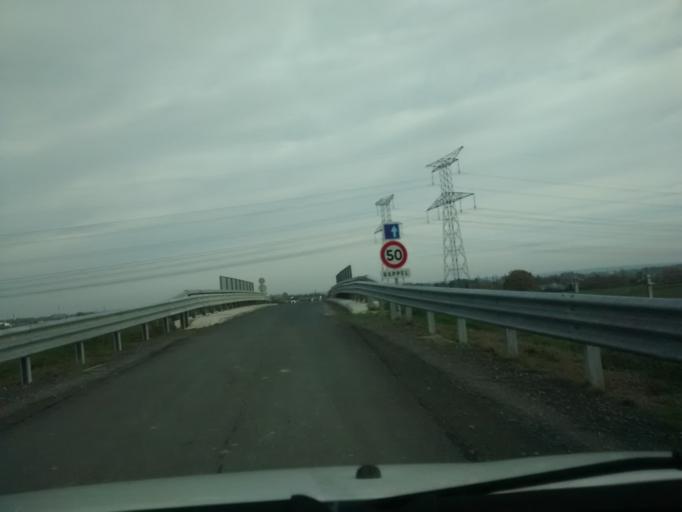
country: FR
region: Brittany
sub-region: Departement d'Ille-et-Vilaine
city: Noyal-sur-Vilaine
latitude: 48.0885
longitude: -1.5299
